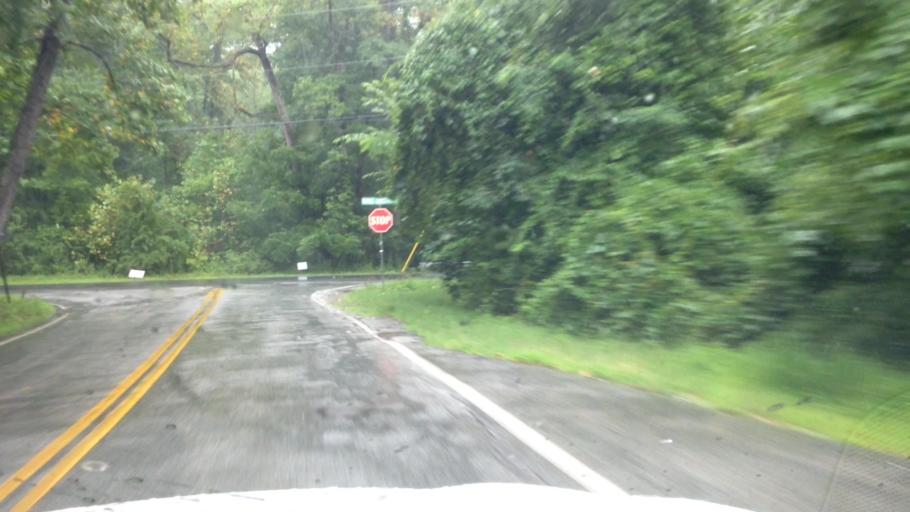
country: US
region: Maryland
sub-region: Anne Arundel County
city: Odenton
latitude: 39.1023
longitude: -76.6862
